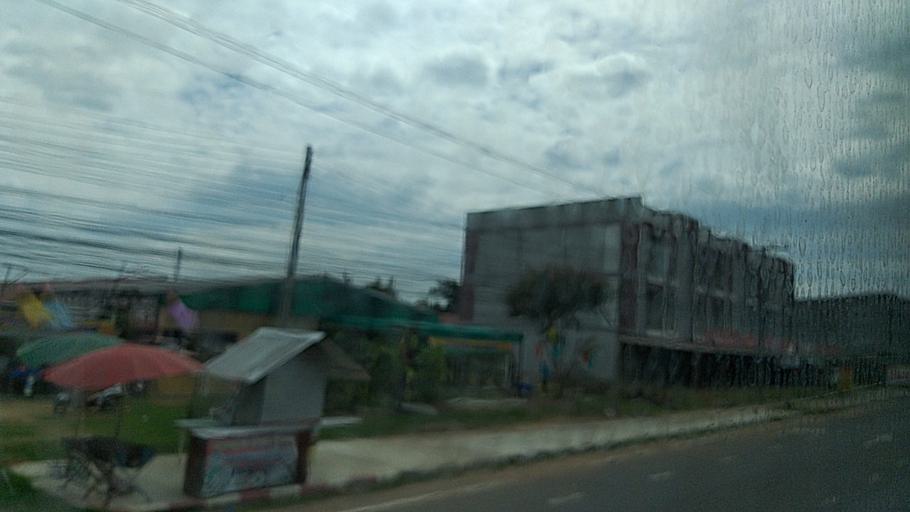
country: TH
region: Maha Sarakham
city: Maha Sarakham
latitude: 16.2505
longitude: 103.2751
